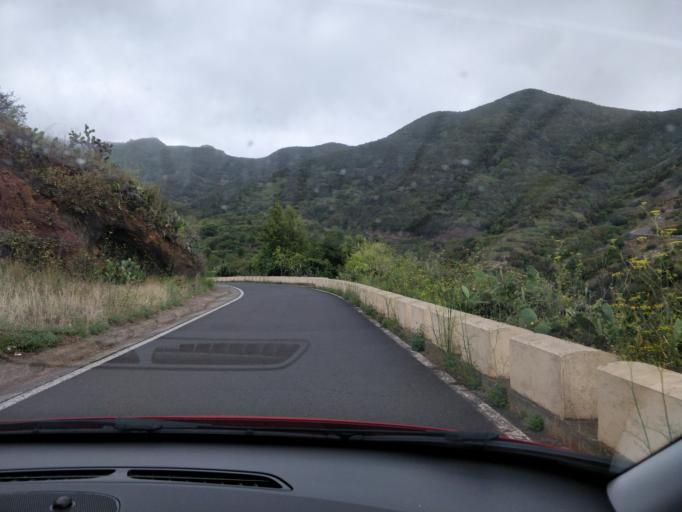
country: ES
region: Canary Islands
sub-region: Provincia de Santa Cruz de Tenerife
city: Tanque
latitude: 28.3257
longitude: -16.8458
